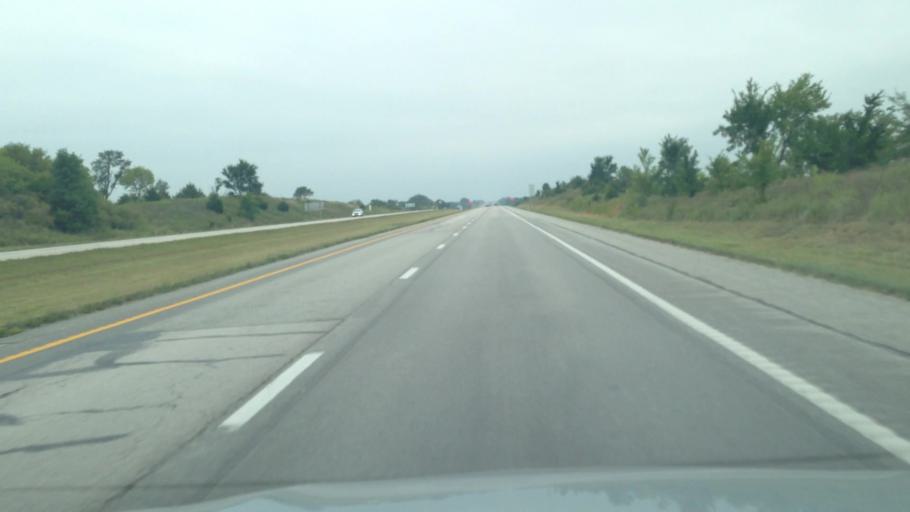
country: US
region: Iowa
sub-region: Decatur County
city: Lamoni
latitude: 40.4590
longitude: -93.9792
